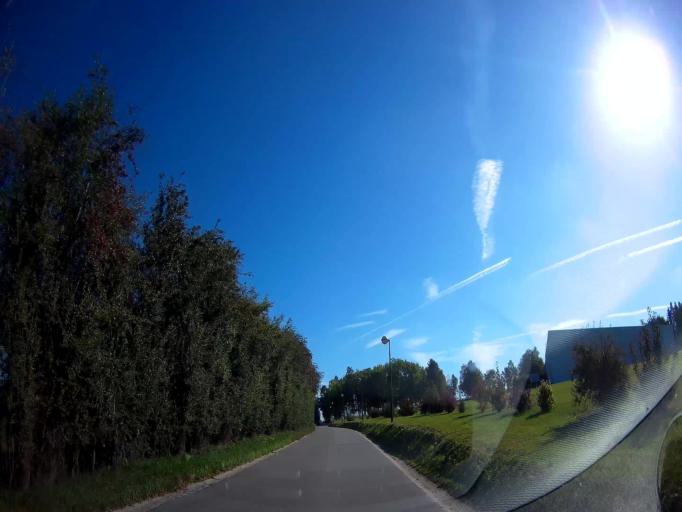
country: BE
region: Wallonia
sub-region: Province du Luxembourg
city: Bastogne
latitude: 50.0110
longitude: 5.7370
